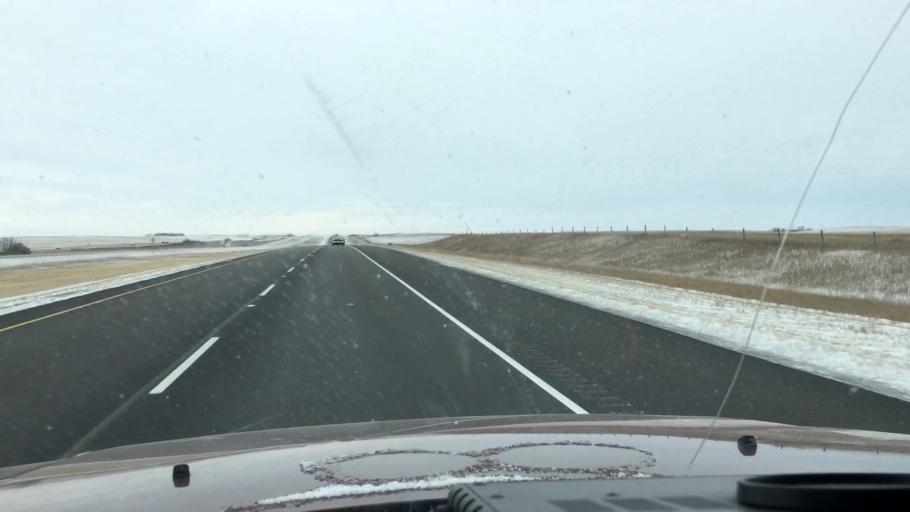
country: CA
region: Saskatchewan
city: Saskatoon
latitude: 51.7177
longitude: -106.4683
